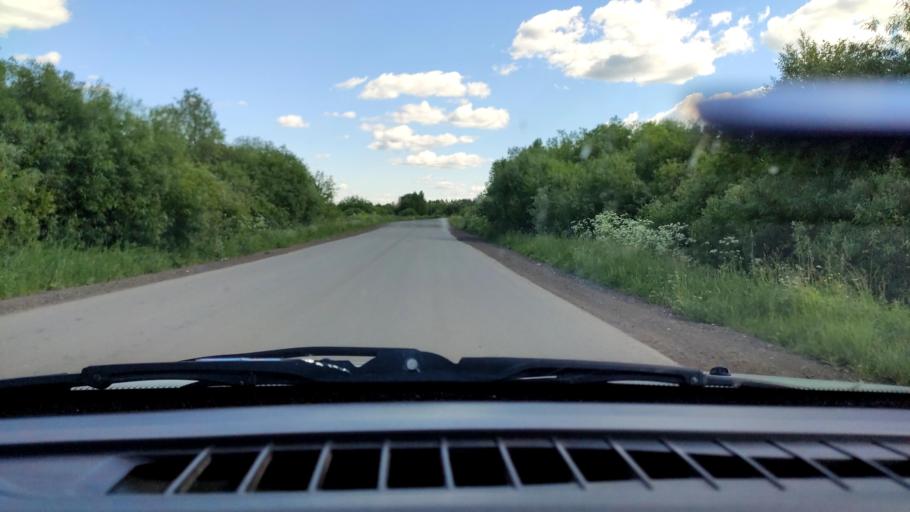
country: RU
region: Perm
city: Uinskoye
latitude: 57.1645
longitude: 56.5683
